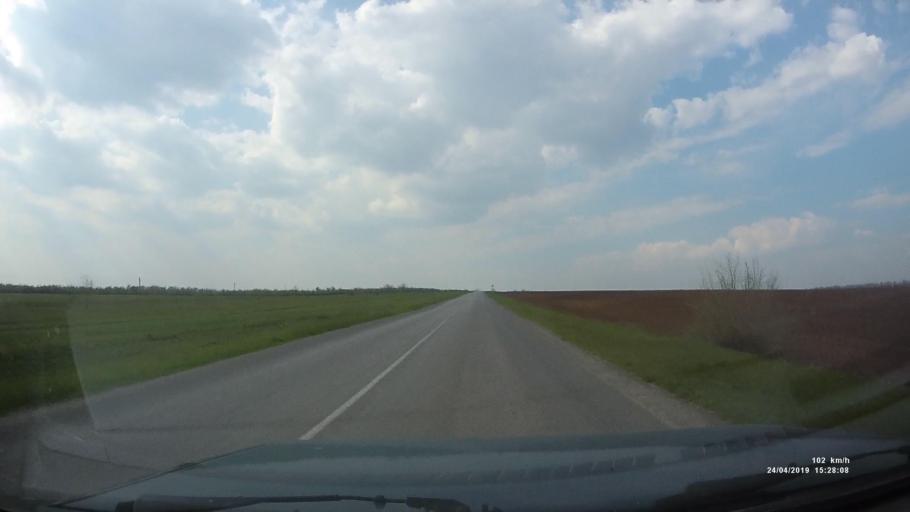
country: RU
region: Rostov
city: Remontnoye
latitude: 46.5747
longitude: 43.0206
